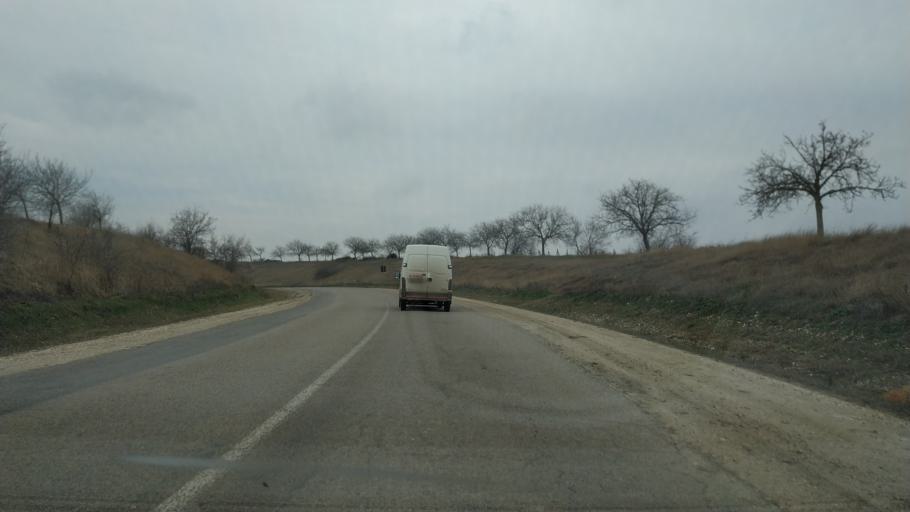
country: MD
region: Cahul
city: Cahul
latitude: 45.9597
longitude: 28.3895
